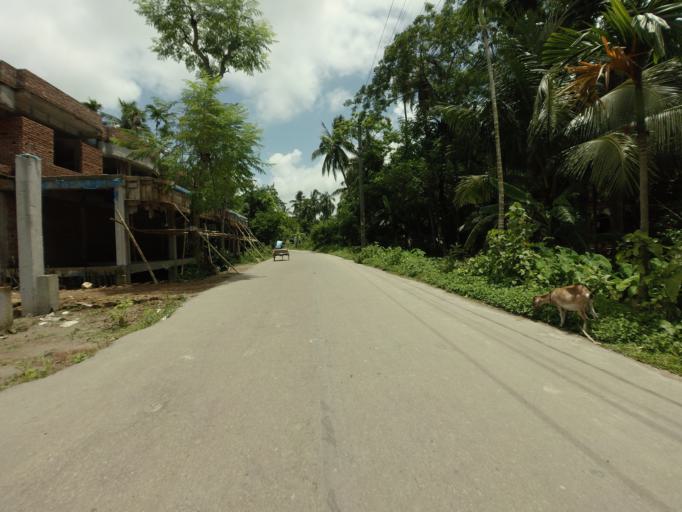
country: BD
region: Khulna
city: Kalia
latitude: 23.0337
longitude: 89.6324
